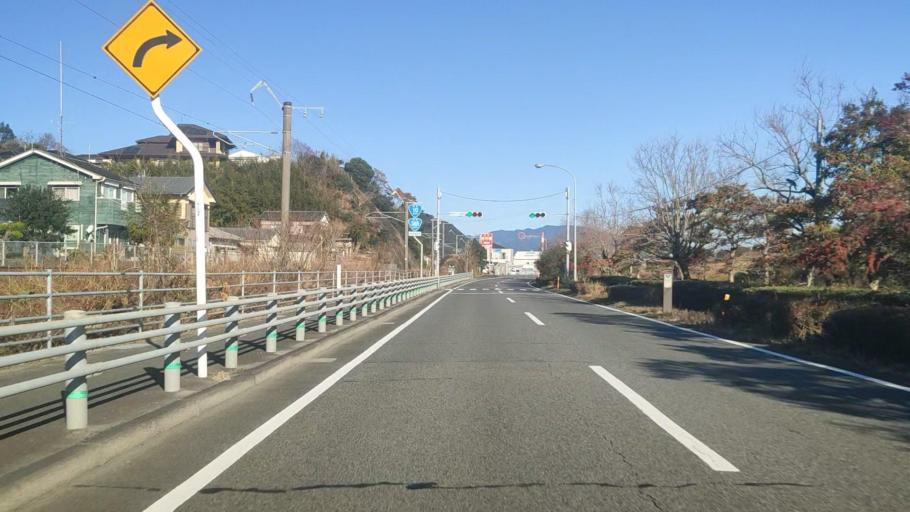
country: JP
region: Miyazaki
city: Nobeoka
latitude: 32.5390
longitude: 131.6788
